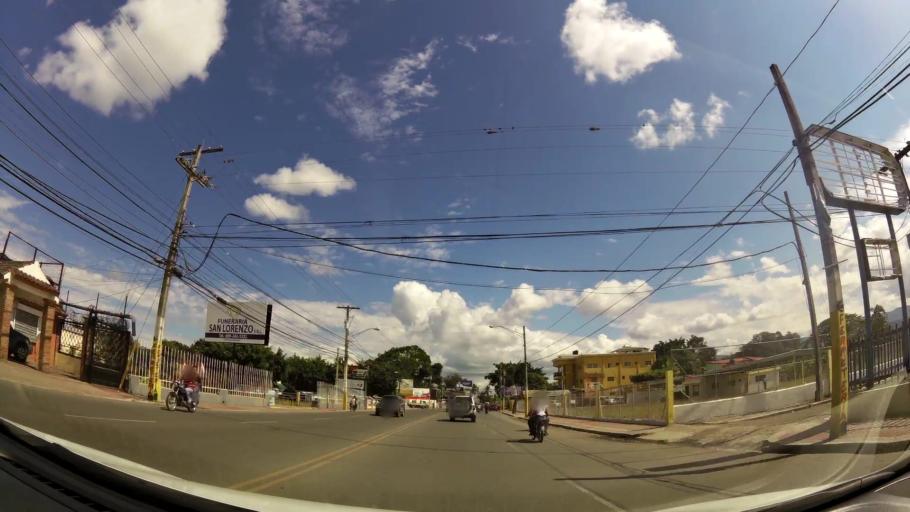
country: DO
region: La Vega
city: Concepcion de La Vega
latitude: 19.2346
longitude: -70.5314
